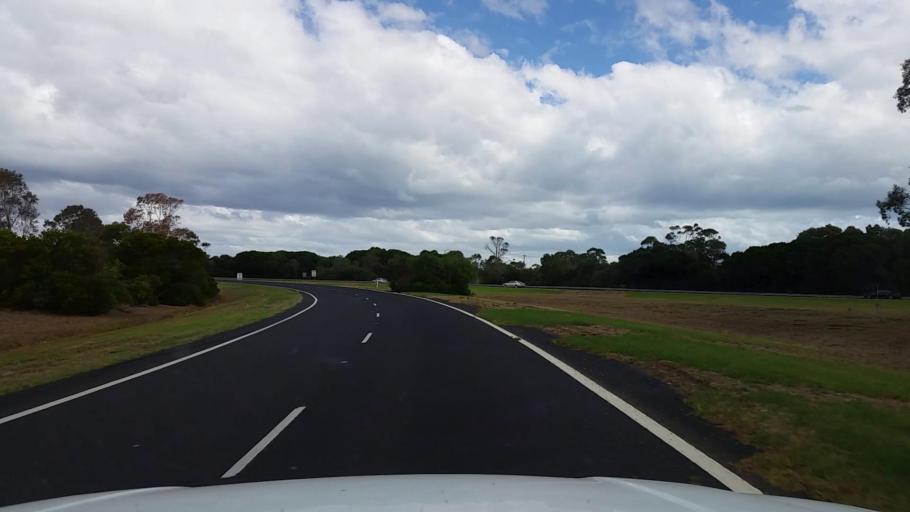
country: AU
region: Victoria
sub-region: Kingston
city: Patterson Lakes
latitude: -38.0682
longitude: 145.1518
